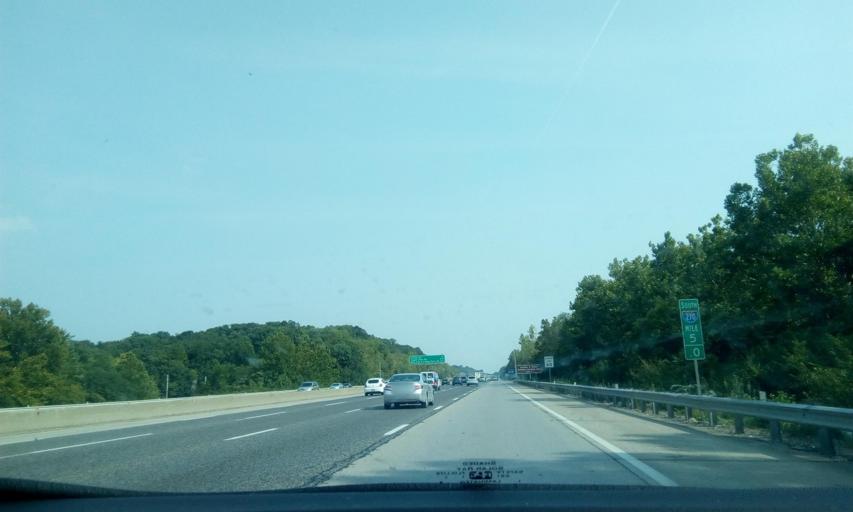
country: US
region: Missouri
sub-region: Saint Louis County
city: Sunset Hills
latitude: 38.5380
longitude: -90.4156
